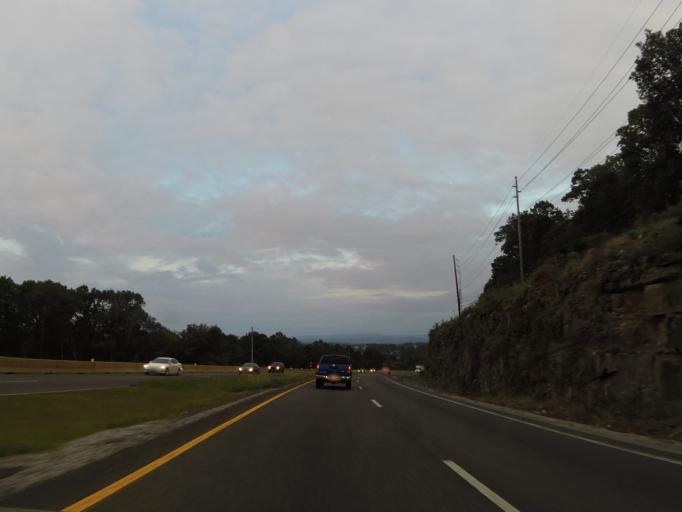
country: US
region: Alabama
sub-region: Madison County
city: Huntsville
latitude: 34.7732
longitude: -86.5469
